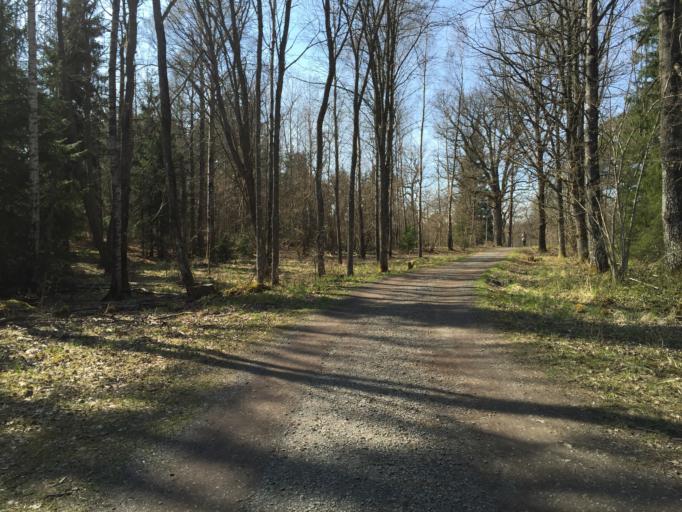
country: SE
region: Stockholm
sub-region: Nacka Kommun
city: Alta
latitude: 59.2698
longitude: 18.1538
